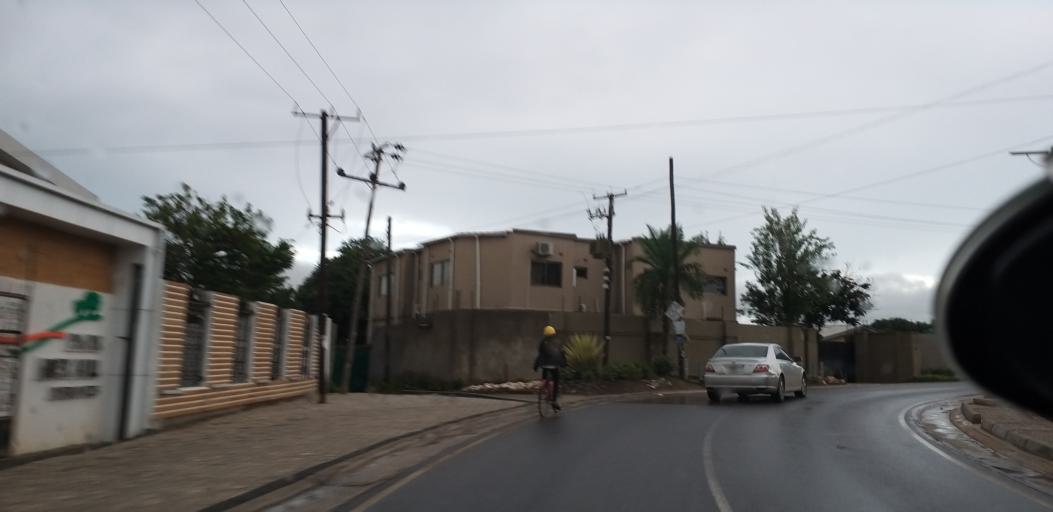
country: ZM
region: Lusaka
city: Lusaka
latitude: -15.4159
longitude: 28.3632
